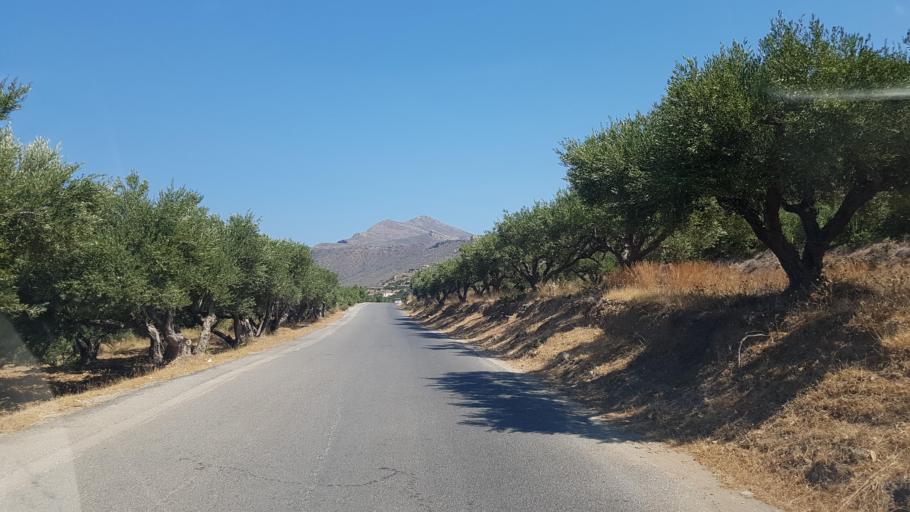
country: GR
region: Crete
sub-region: Nomos Chanias
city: Platanos
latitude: 35.4874
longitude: 23.5889
